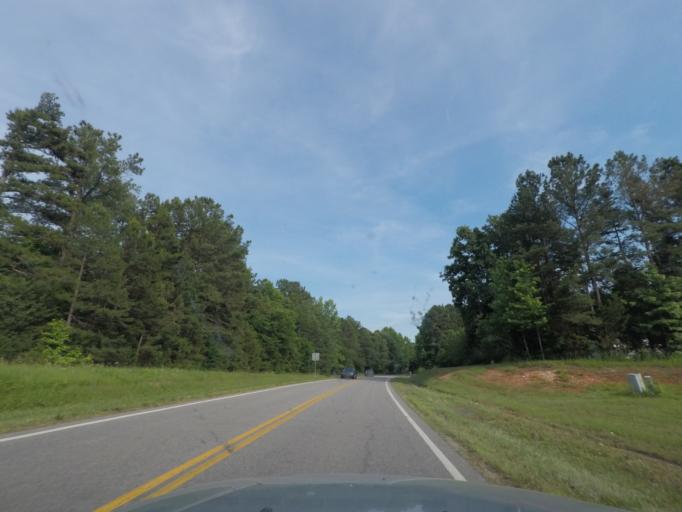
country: US
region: Virginia
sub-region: Mecklenburg County
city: Clarksville
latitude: 36.5989
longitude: -78.5508
